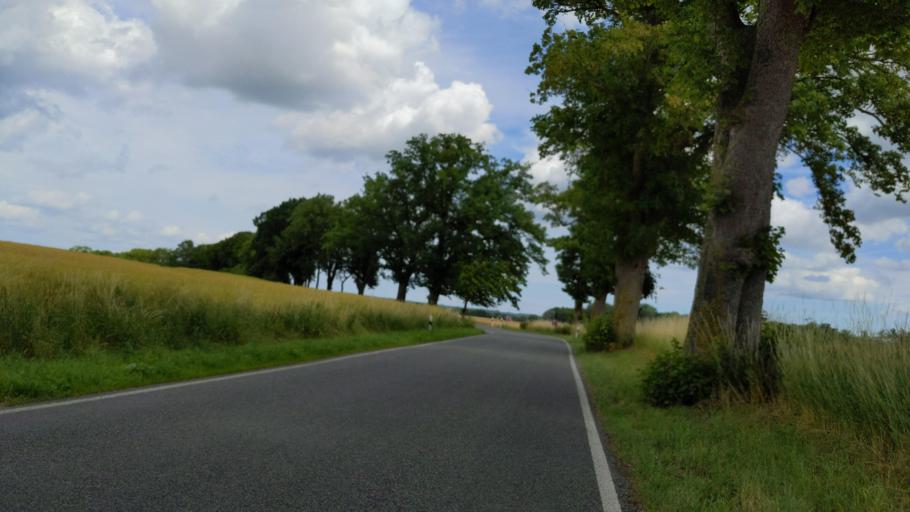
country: DE
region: Mecklenburg-Vorpommern
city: Dassow
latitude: 53.9351
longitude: 10.9698
